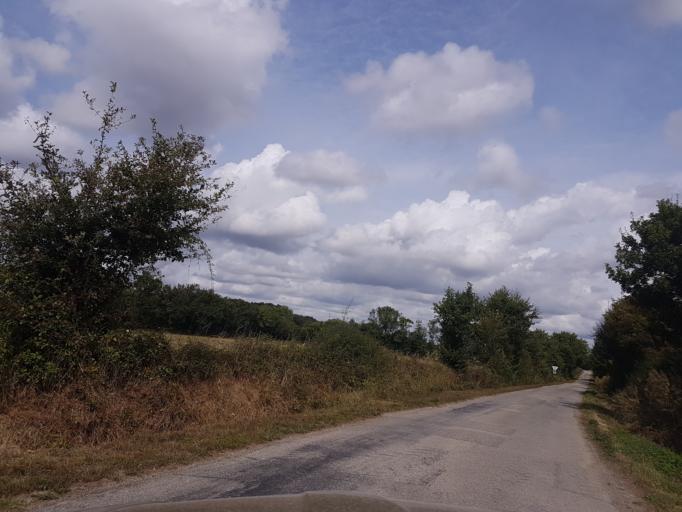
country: FR
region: Pays de la Loire
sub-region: Departement de la Loire-Atlantique
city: Petit-Mars
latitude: 47.4122
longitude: -1.4470
